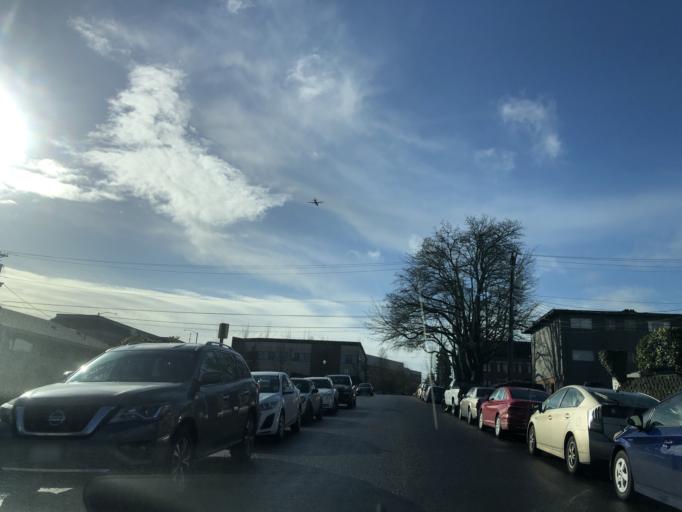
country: US
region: Washington
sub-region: Pierce County
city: Tacoma
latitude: 47.2618
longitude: -122.4538
